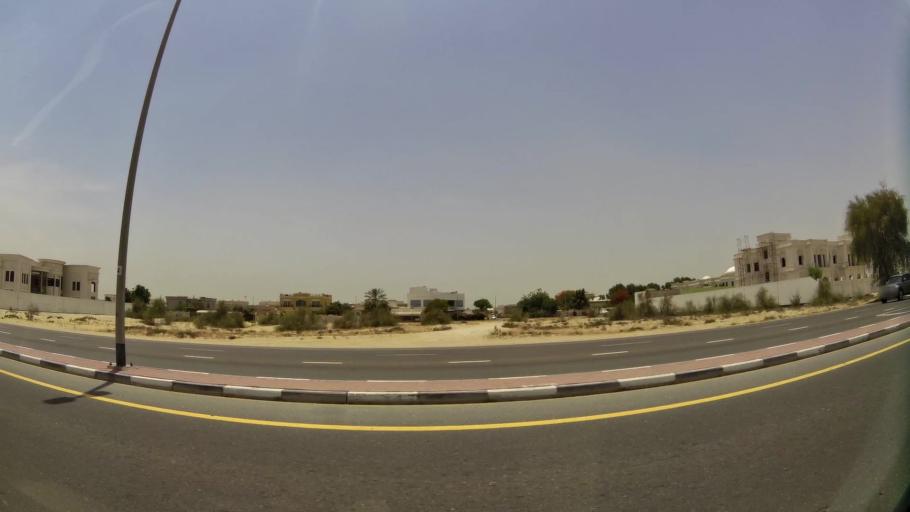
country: AE
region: Ash Shariqah
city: Sharjah
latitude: 25.2407
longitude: 55.4674
